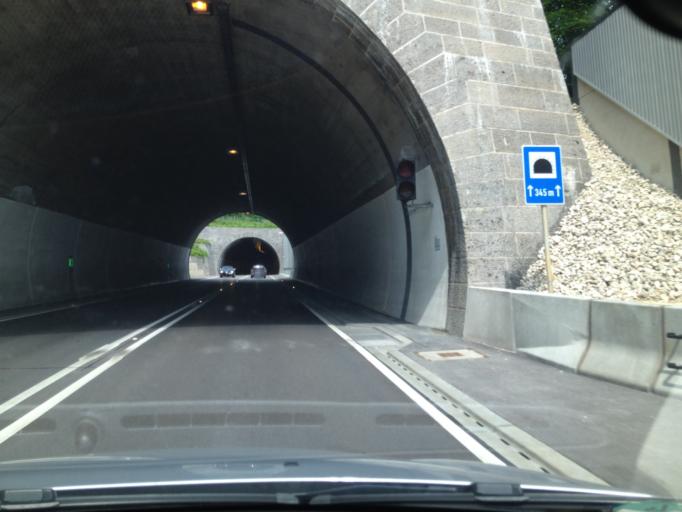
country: DE
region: Bavaria
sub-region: Swabia
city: Harburg
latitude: 48.7835
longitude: 10.6894
